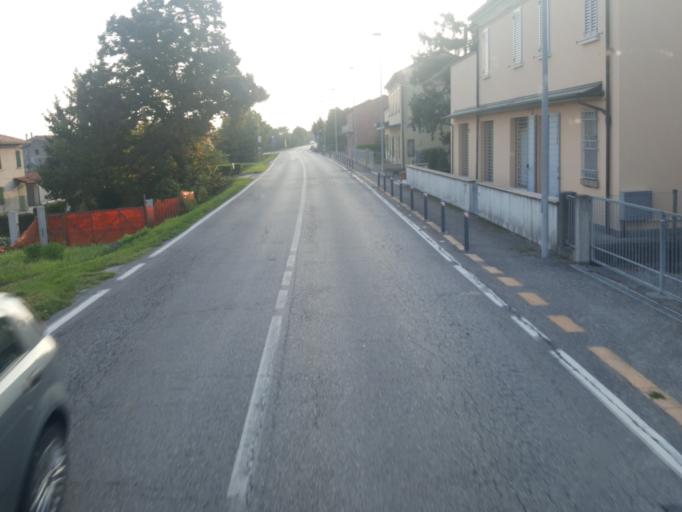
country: IT
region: Emilia-Romagna
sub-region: Provincia di Ferrara
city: San Biagio
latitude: 44.5845
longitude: 11.9094
